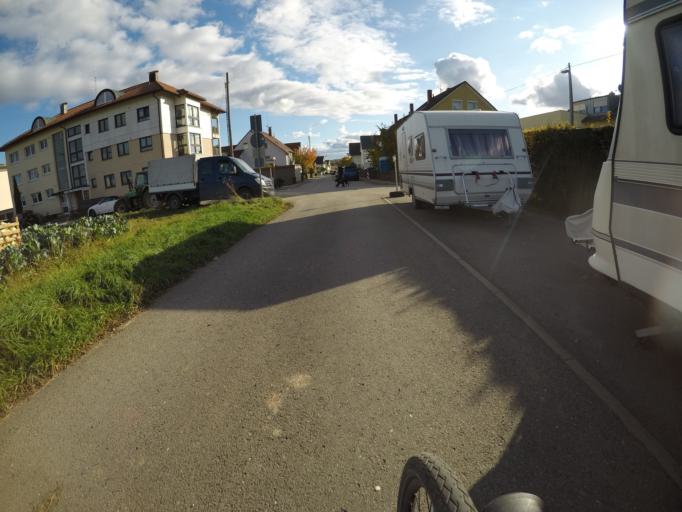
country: DE
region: Baden-Wuerttemberg
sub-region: Regierungsbezirk Stuttgart
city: Filderstadt
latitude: 48.6837
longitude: 9.2203
